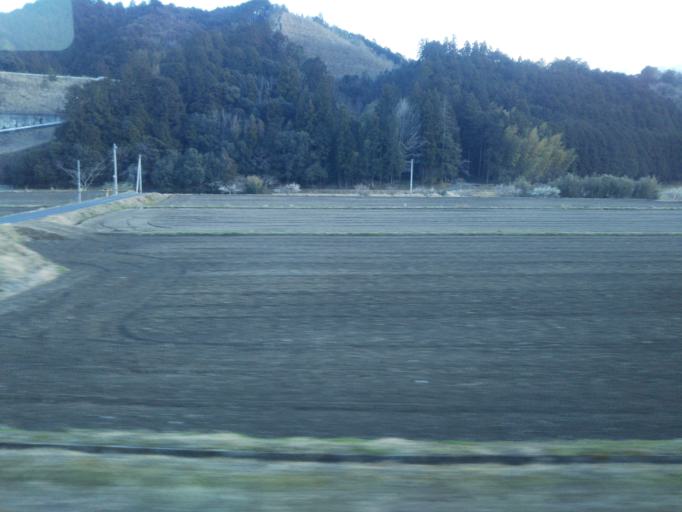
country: JP
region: Kochi
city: Susaki
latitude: 33.2769
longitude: 133.1784
